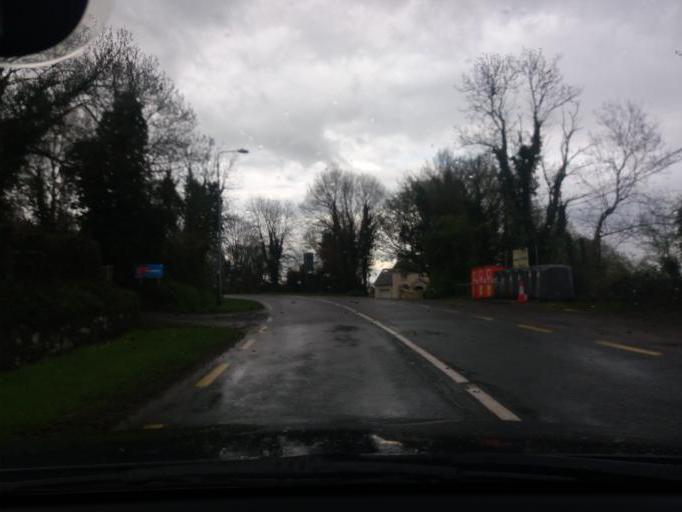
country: IE
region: Ulster
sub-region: An Cabhan
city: Ballyconnell
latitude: 54.1193
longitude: -7.6711
